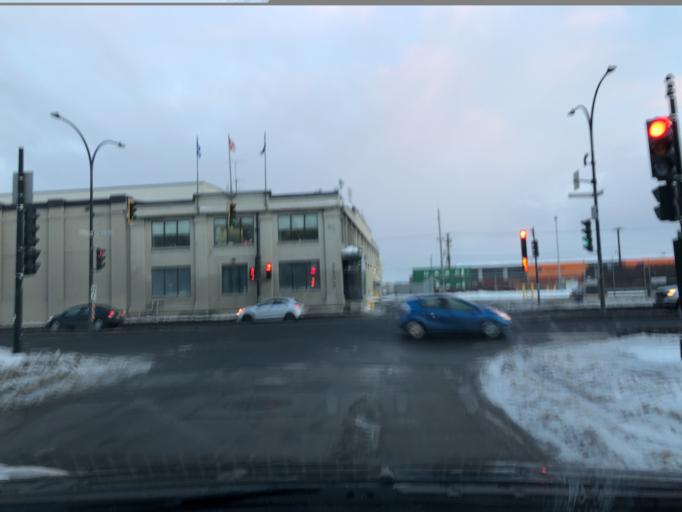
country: CA
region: Quebec
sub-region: Monteregie
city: Longueuil
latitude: 45.5407
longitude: -73.5385
